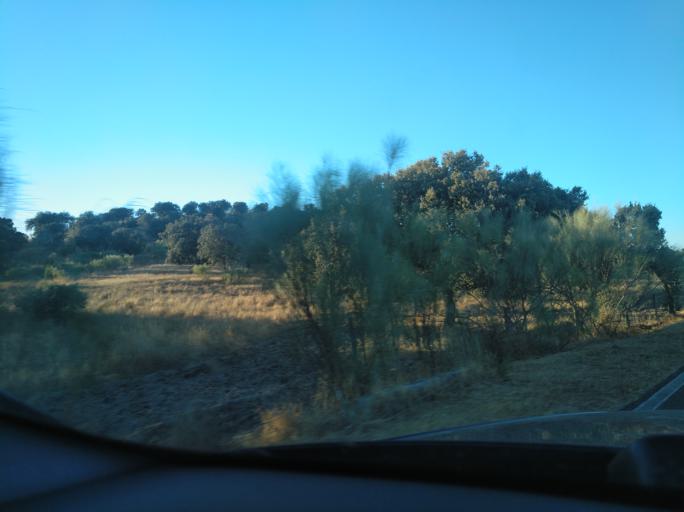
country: PT
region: Portalegre
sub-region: Arronches
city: Arronches
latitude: 39.0693
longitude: -7.2422
